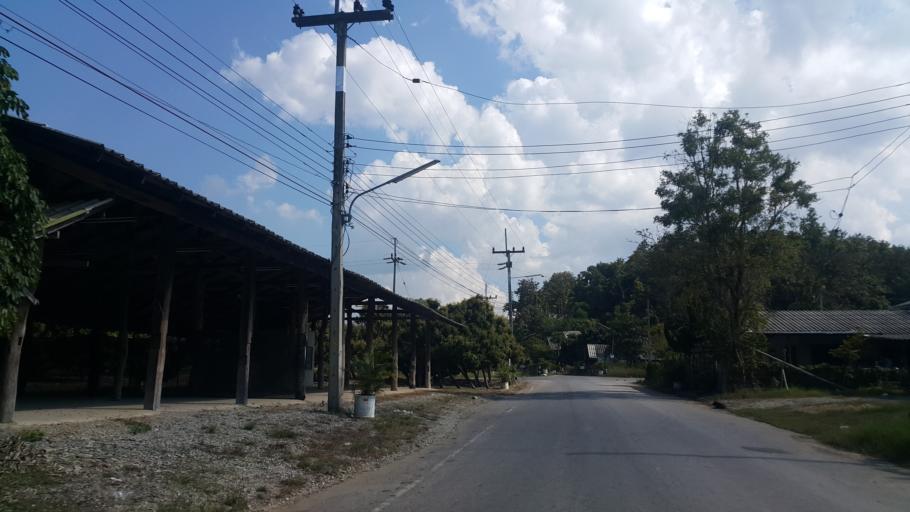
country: TH
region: Lamphun
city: Ban Thi
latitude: 18.6215
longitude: 99.1605
